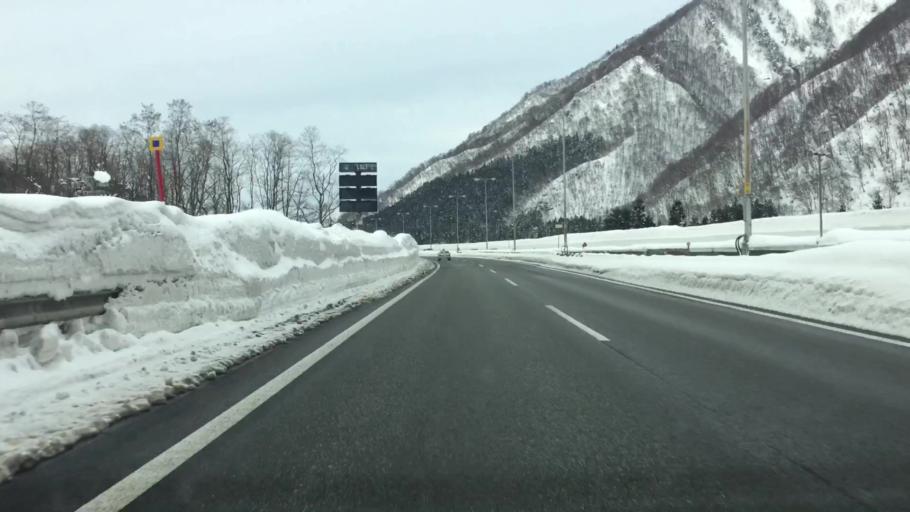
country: JP
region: Niigata
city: Shiozawa
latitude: 36.8720
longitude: 138.8646
